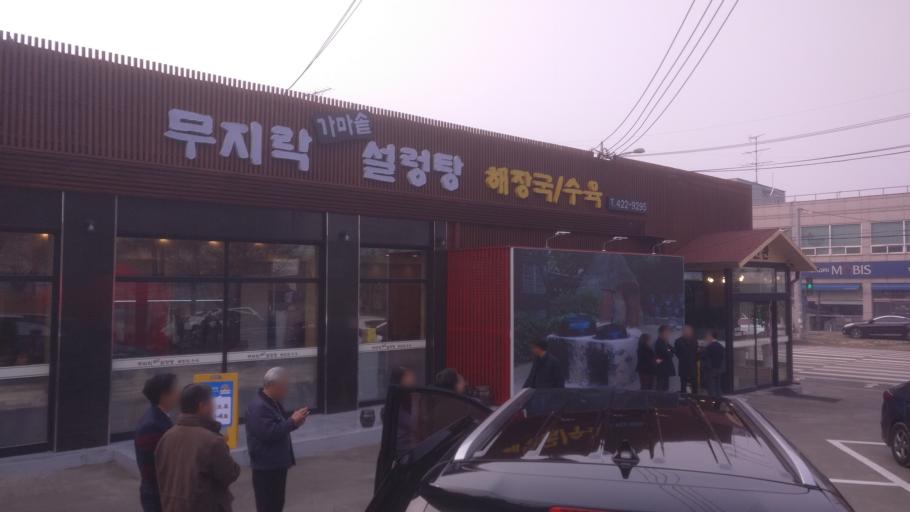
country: KR
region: Incheon
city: Incheon
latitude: 37.3971
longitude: 126.7162
